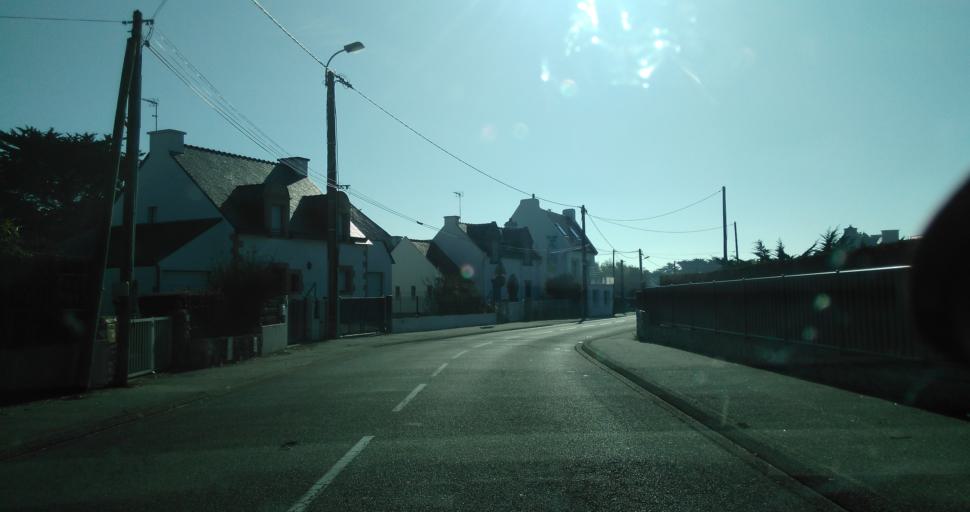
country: FR
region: Brittany
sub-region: Departement du Morbihan
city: Saint-Pierre-Quiberon
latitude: 47.5359
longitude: -3.1395
